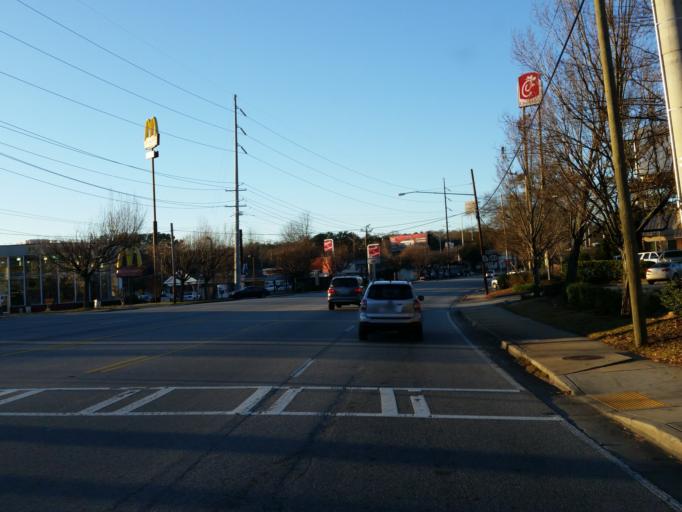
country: US
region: Georgia
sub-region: Cobb County
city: Vinings
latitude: 33.8467
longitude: -84.4285
